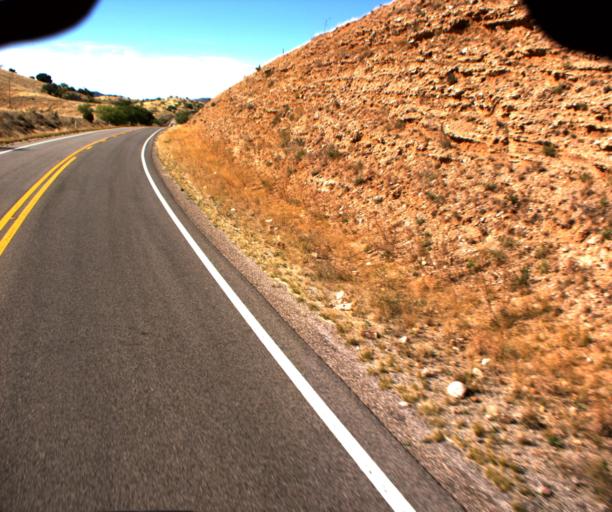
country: US
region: Arizona
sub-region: Pima County
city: Corona de Tucson
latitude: 31.8051
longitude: -110.7075
